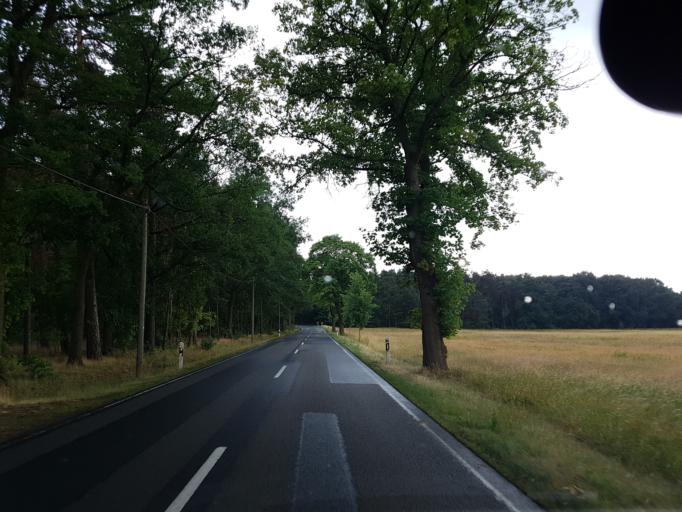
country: DE
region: Saxony-Anhalt
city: Seyda
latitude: 51.8937
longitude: 12.9334
